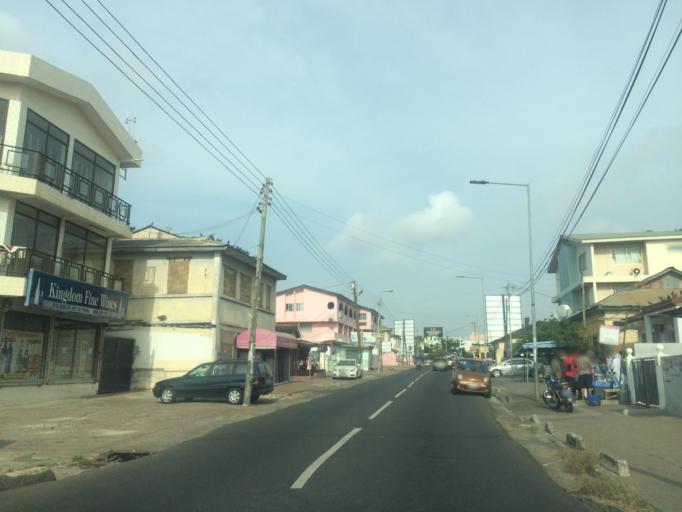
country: GH
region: Greater Accra
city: Accra
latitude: 5.5527
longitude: -0.1884
